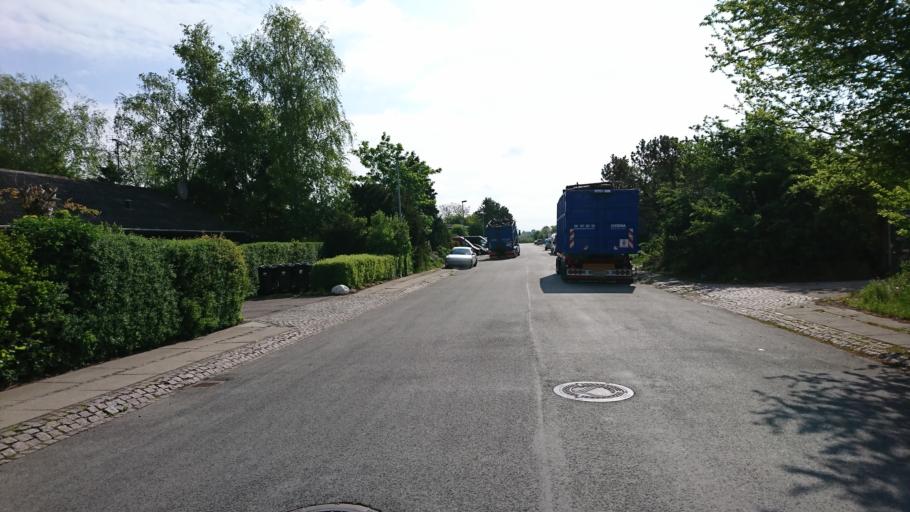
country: DK
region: Capital Region
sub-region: Egedal Kommune
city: Smorumnedre
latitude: 55.7274
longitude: 12.3226
